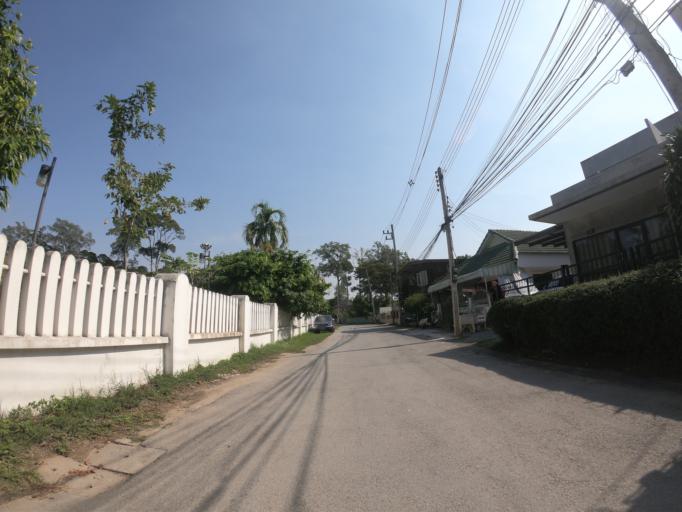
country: TH
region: Chiang Mai
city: Chiang Mai
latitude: 18.7725
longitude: 99.0052
